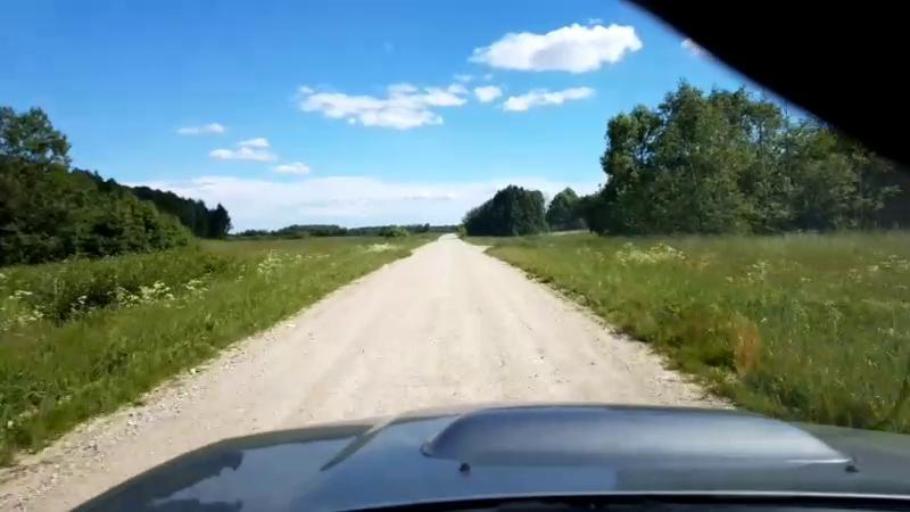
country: EE
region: Paernumaa
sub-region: Sauga vald
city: Sauga
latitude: 58.5064
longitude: 24.5199
